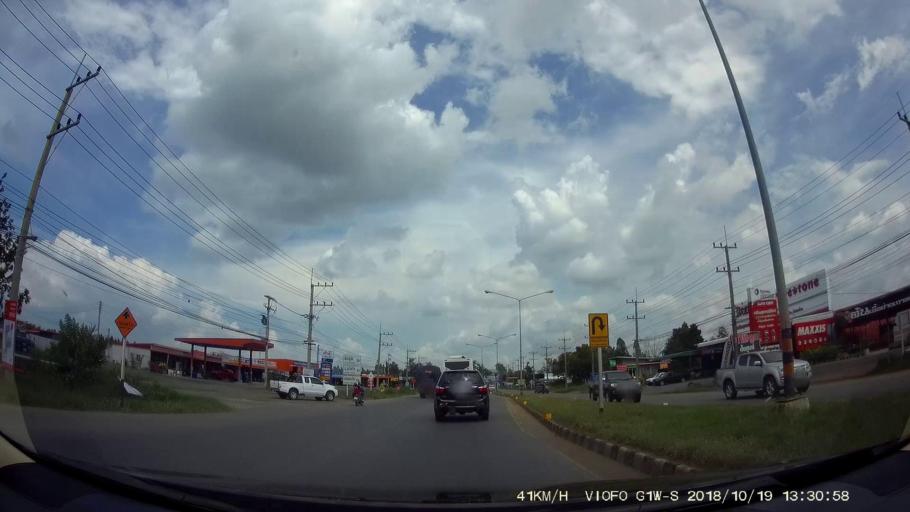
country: TH
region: Chaiyaphum
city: Chatturat
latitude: 15.5750
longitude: 101.8628
